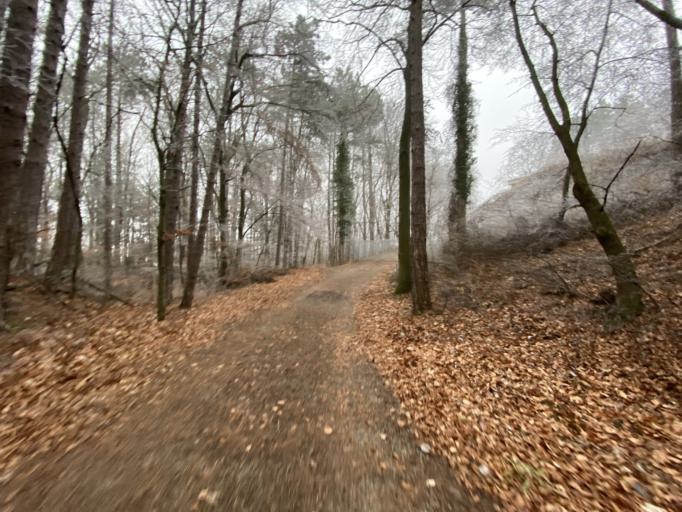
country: AT
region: Lower Austria
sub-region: Politischer Bezirk Baden
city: Baden
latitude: 47.9988
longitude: 16.2005
